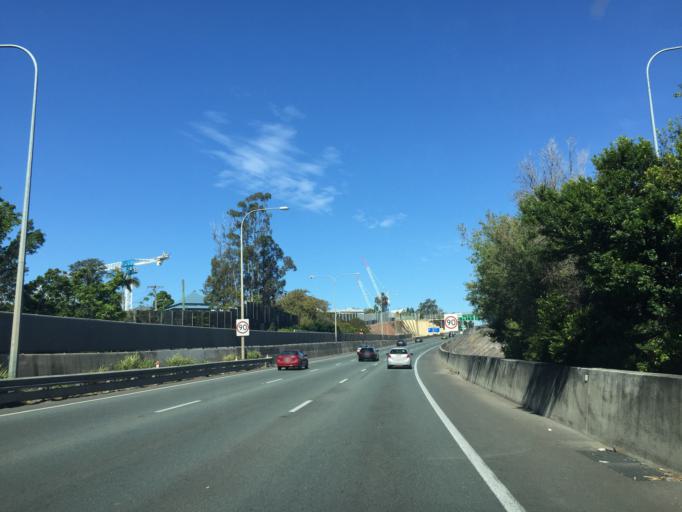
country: AU
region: Queensland
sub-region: Brisbane
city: Woolloongabba
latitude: -27.4932
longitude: 153.0358
